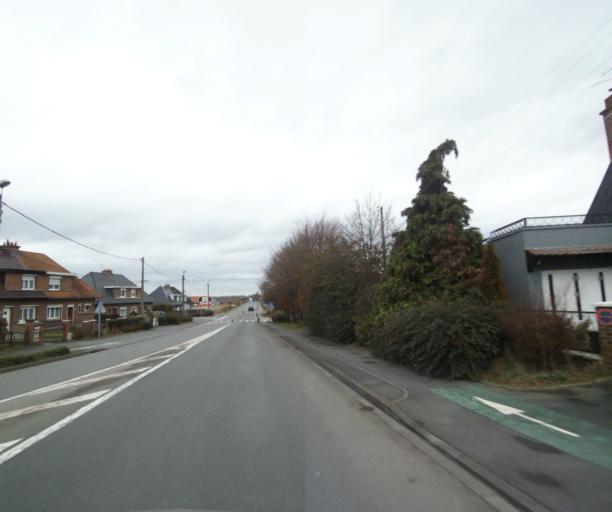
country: FR
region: Nord-Pas-de-Calais
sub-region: Departement du Nord
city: Saint-Saulve
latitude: 50.3756
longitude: 3.5681
